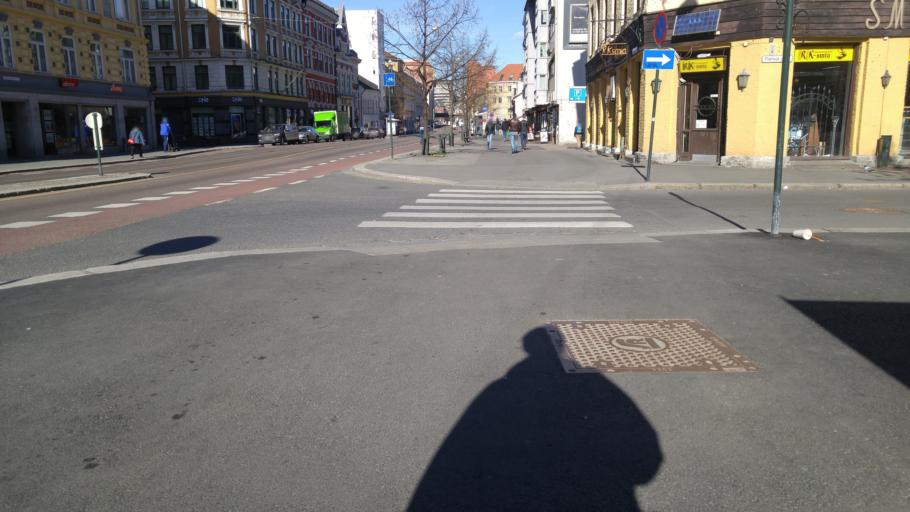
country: NO
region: Oslo
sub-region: Oslo
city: Oslo
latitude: 59.9121
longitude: 10.7661
